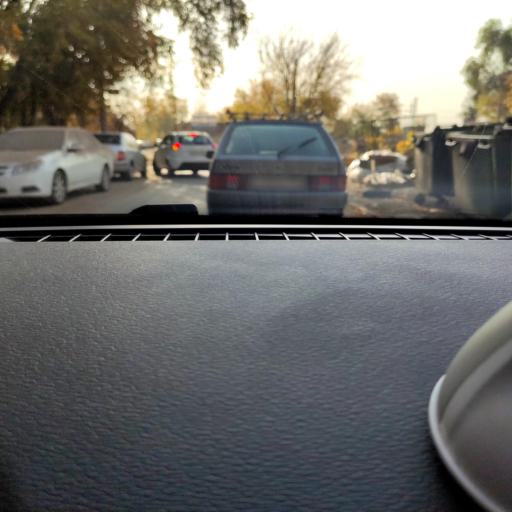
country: RU
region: Samara
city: Smyshlyayevka
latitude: 53.2155
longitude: 50.2711
